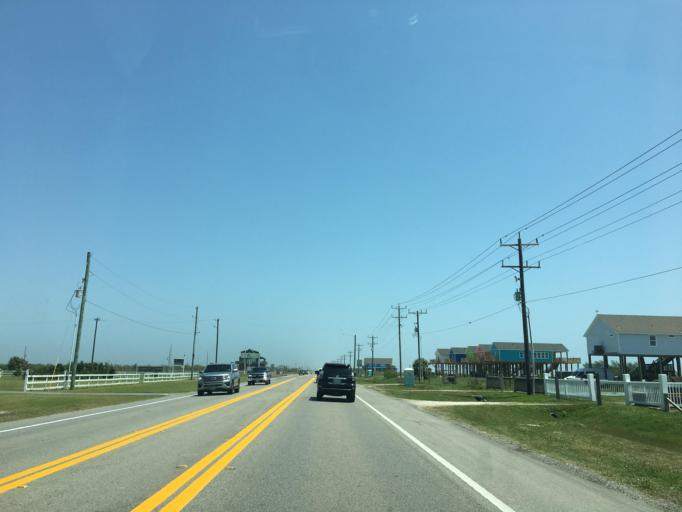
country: US
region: Texas
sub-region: Galveston County
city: Bolivar Peninsula
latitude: 29.5053
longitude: -94.5086
